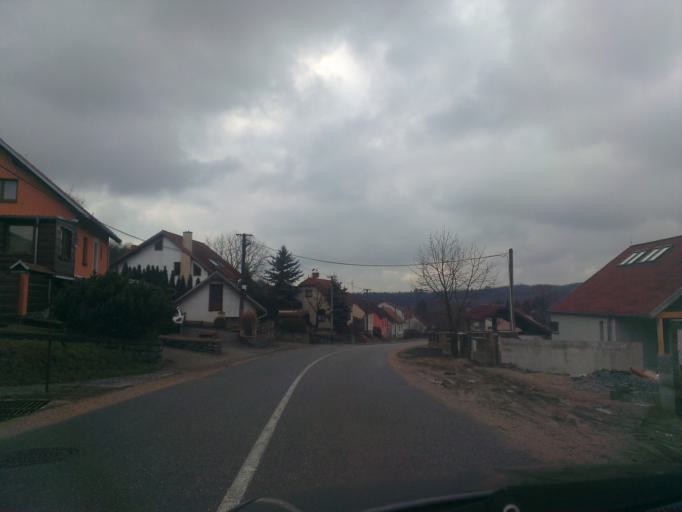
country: CZ
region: South Moravian
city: Bilovice nad Svitavou
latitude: 49.2623
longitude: 16.7209
